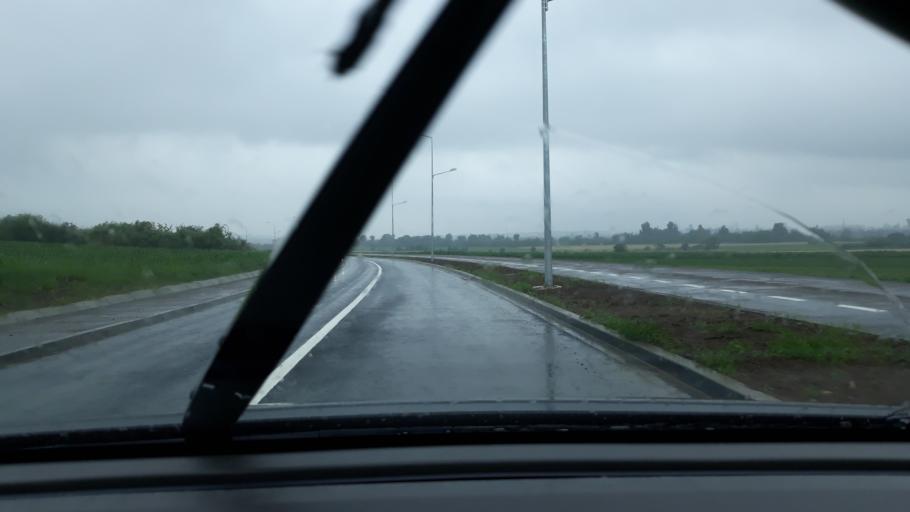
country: RO
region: Bihor
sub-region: Comuna Biharea
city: Oradea
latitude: 47.1048
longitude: 21.9078
